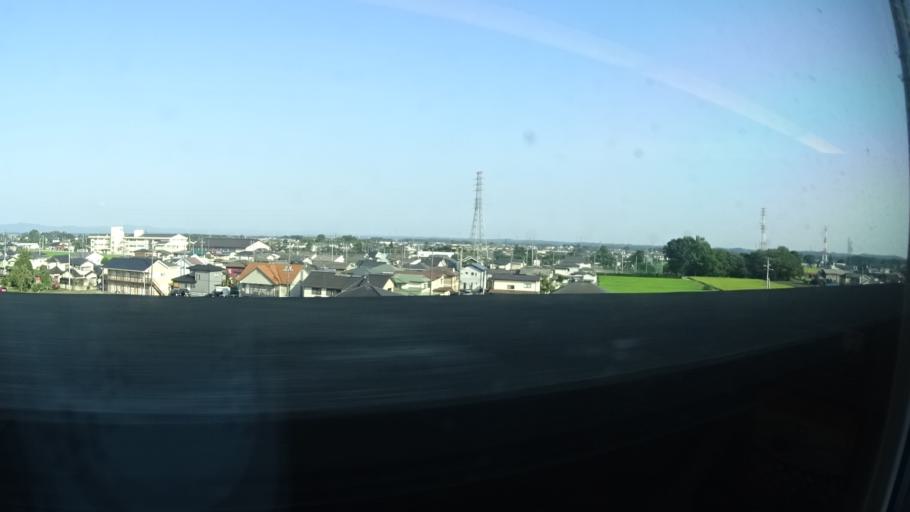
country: JP
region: Tochigi
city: Otawara
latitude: 36.8581
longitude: 139.9681
